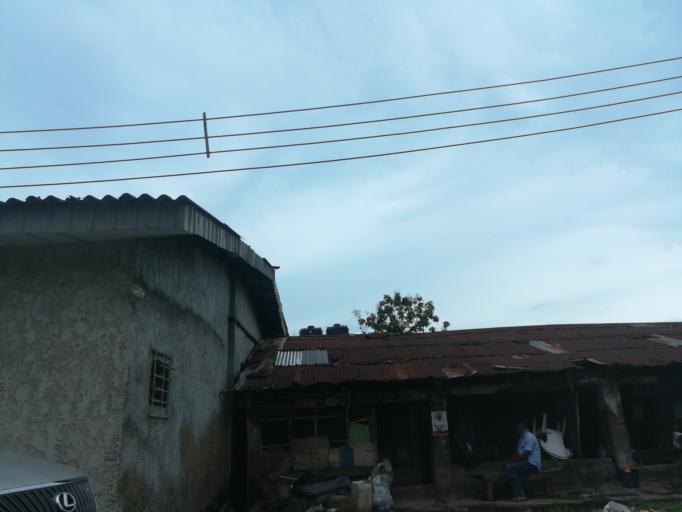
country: NG
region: Lagos
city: Ebute Metta
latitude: 6.4902
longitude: 3.3886
